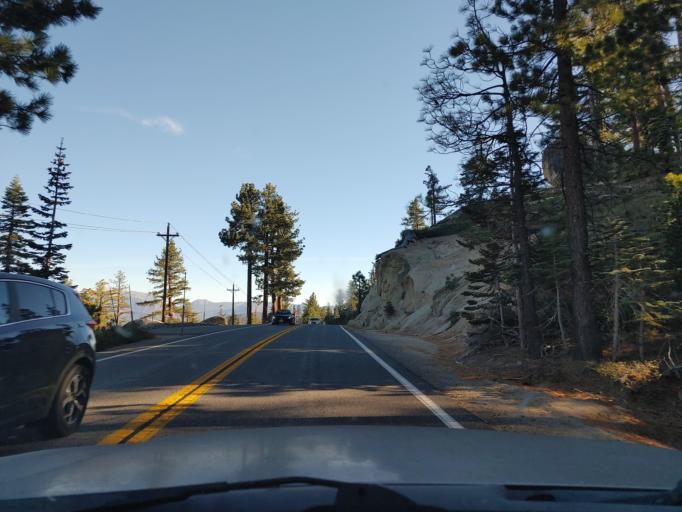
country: US
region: California
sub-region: Placer County
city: Tahoma
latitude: 38.9760
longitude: -120.1008
